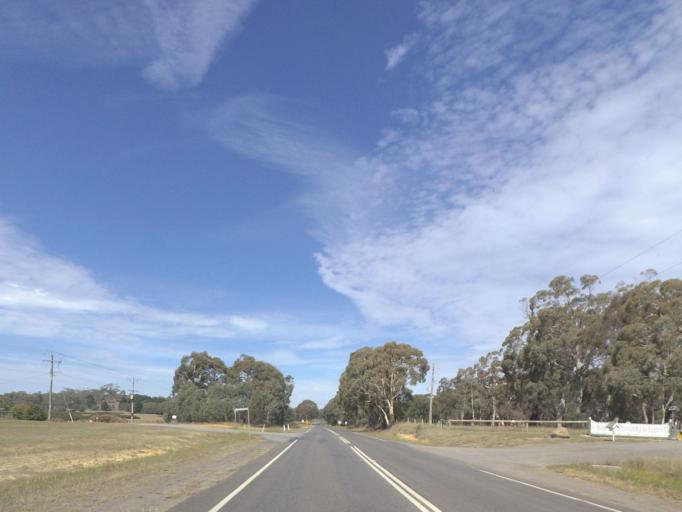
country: AU
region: Victoria
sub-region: Hume
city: Sunbury
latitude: -37.2933
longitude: 144.5076
